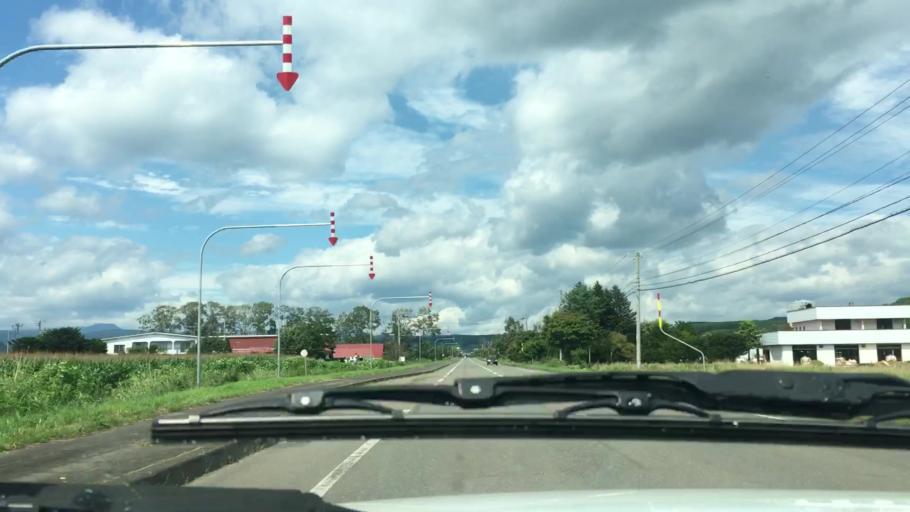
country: JP
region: Hokkaido
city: Otofuke
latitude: 43.2845
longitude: 143.3067
